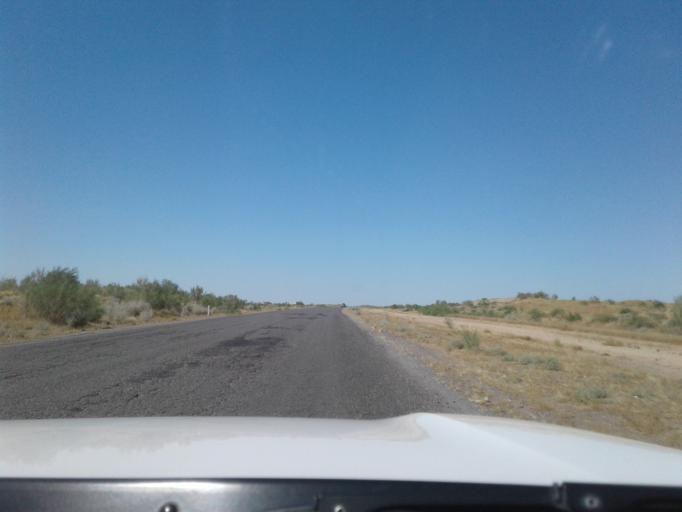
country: TM
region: Mary
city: Bayramaly
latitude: 38.0304
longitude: 62.7493
